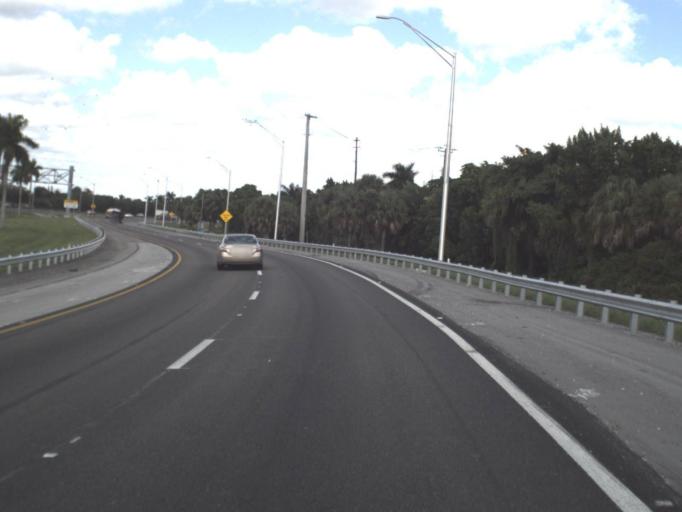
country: US
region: Florida
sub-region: Broward County
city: Miramar
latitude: 25.9757
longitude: -80.2284
